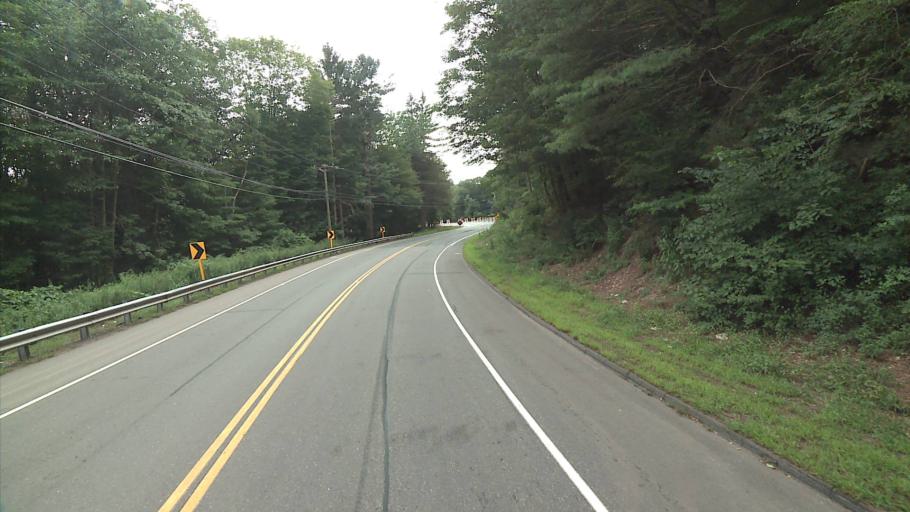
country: US
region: Connecticut
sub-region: Tolland County
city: Tolland
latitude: 41.8840
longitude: -72.3084
